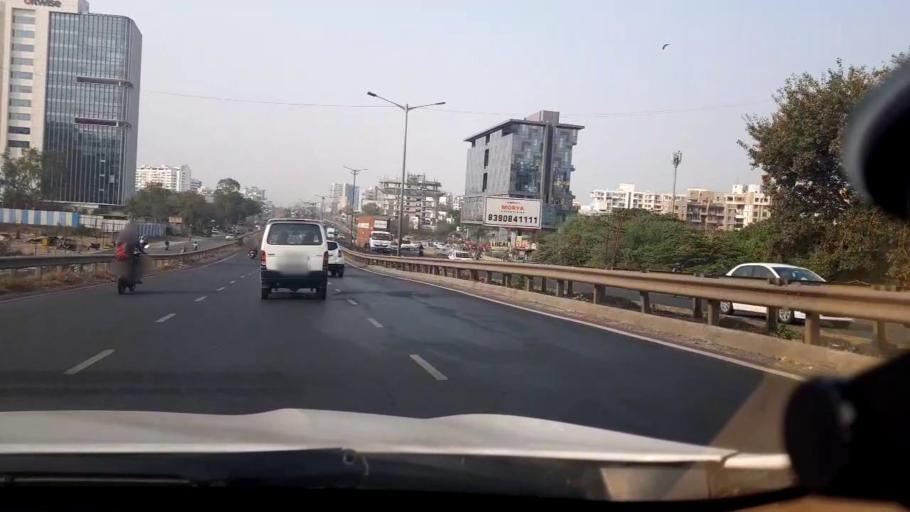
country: IN
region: Maharashtra
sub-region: Pune Division
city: Pimpri
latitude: 18.5551
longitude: 73.7707
